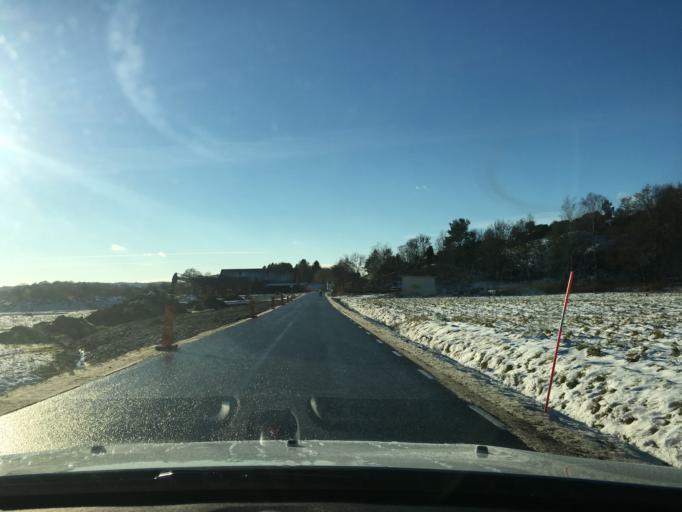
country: SE
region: Vaestra Goetaland
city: Svanesund
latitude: 58.1428
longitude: 11.7934
